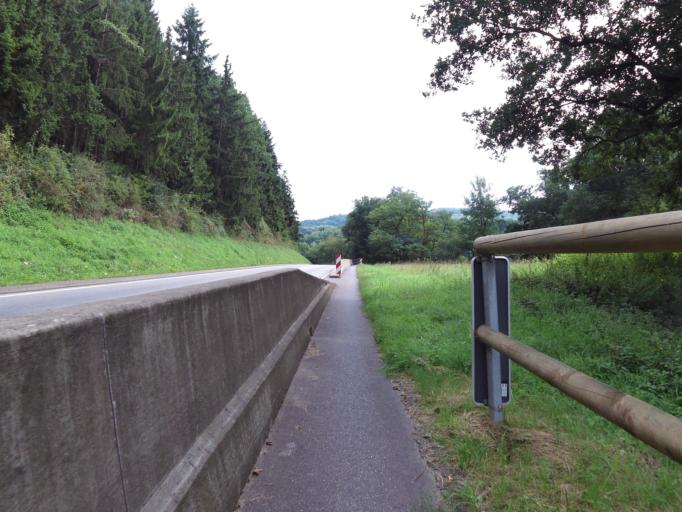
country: DE
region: Rheinland-Pfalz
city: Schweisweiler
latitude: 49.5921
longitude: 7.8163
